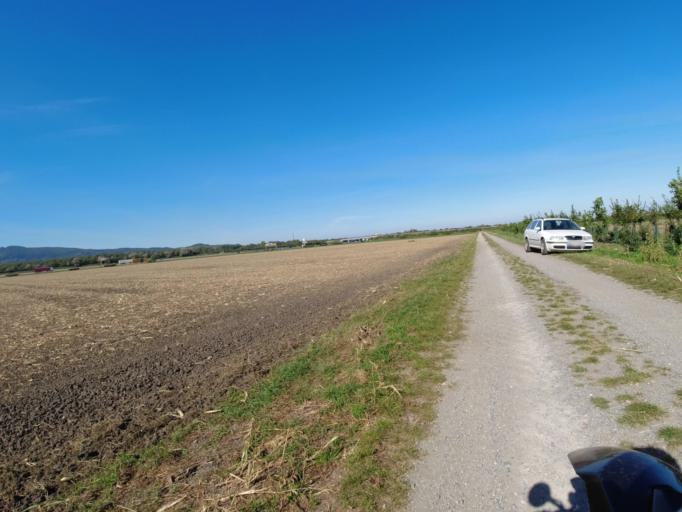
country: AT
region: Lower Austria
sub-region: Politischer Bezirk Baden
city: Trumau
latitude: 48.0235
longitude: 16.3386
